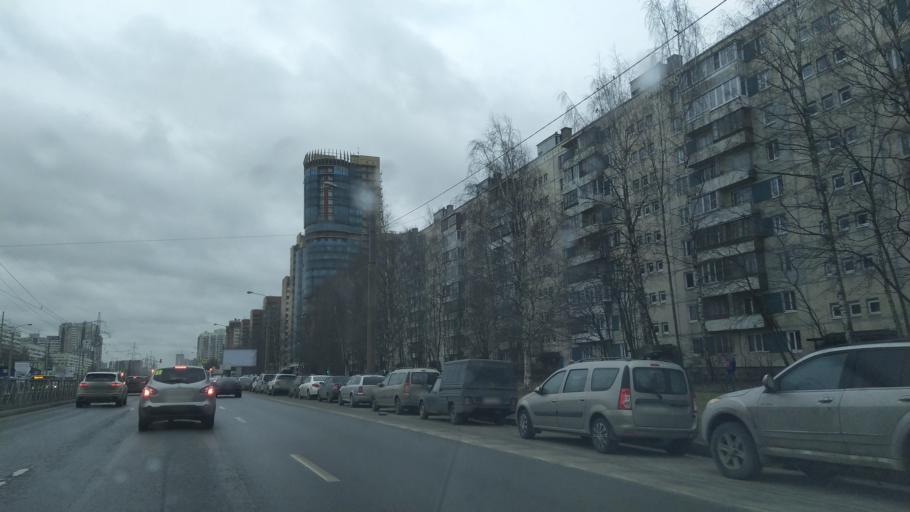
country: RU
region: St.-Petersburg
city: Komendantsky aerodrom
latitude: 60.0057
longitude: 30.2784
